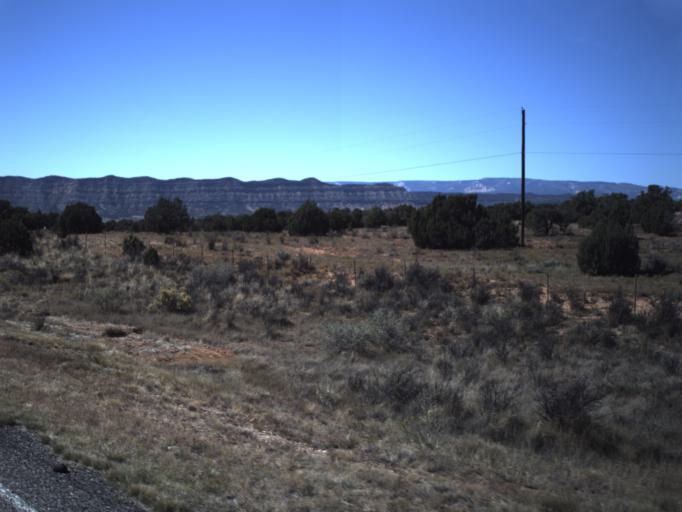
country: US
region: Utah
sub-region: Wayne County
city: Loa
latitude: 37.7333
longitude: -111.5146
